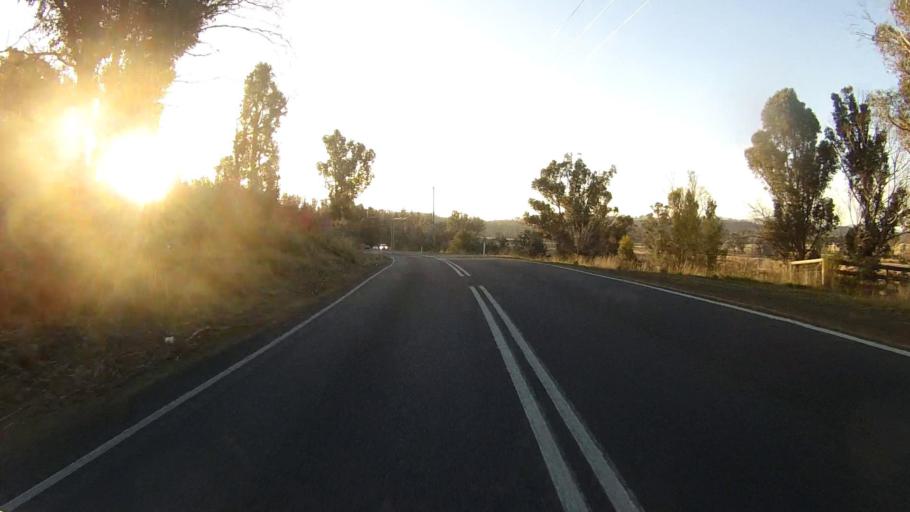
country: AU
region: Tasmania
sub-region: Sorell
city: Sorell
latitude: -42.8729
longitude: 147.8237
